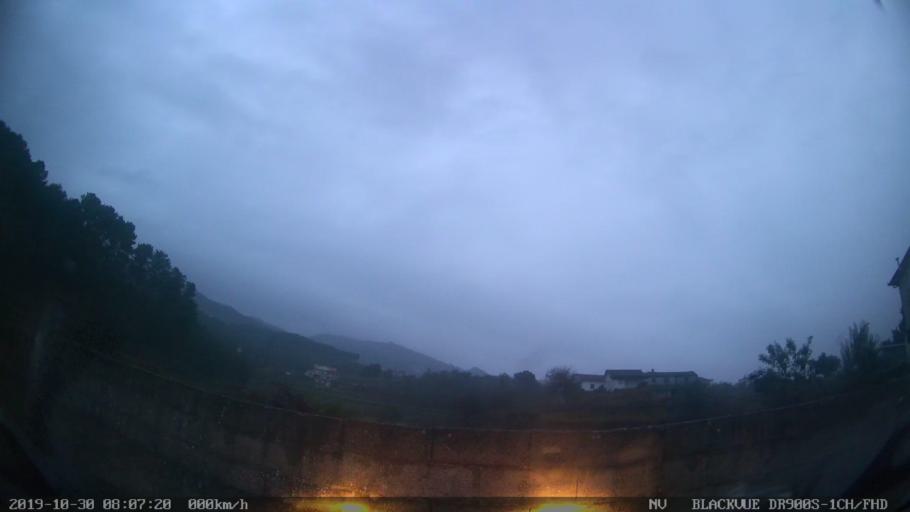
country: PT
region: Vila Real
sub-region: Vila Real
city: Vila Real
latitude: 41.3147
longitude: -7.7735
